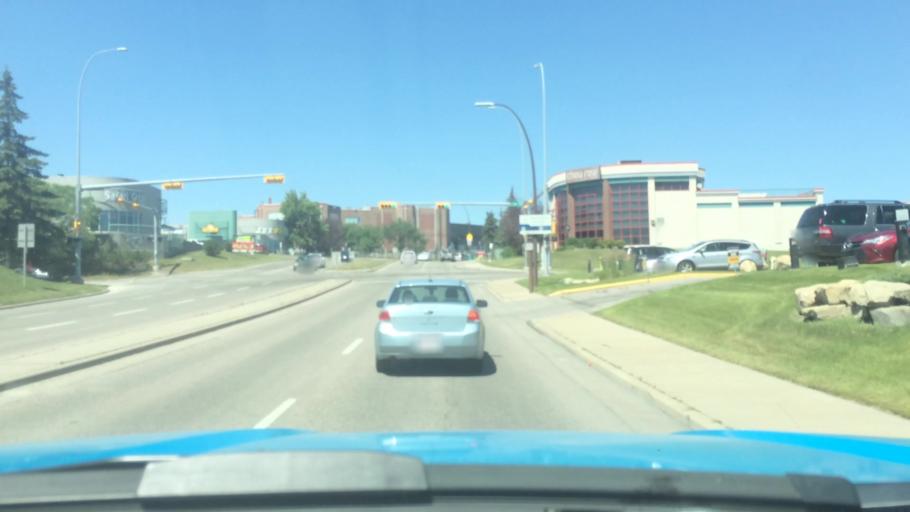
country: CA
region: Alberta
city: Calgary
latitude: 51.0496
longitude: -113.9917
